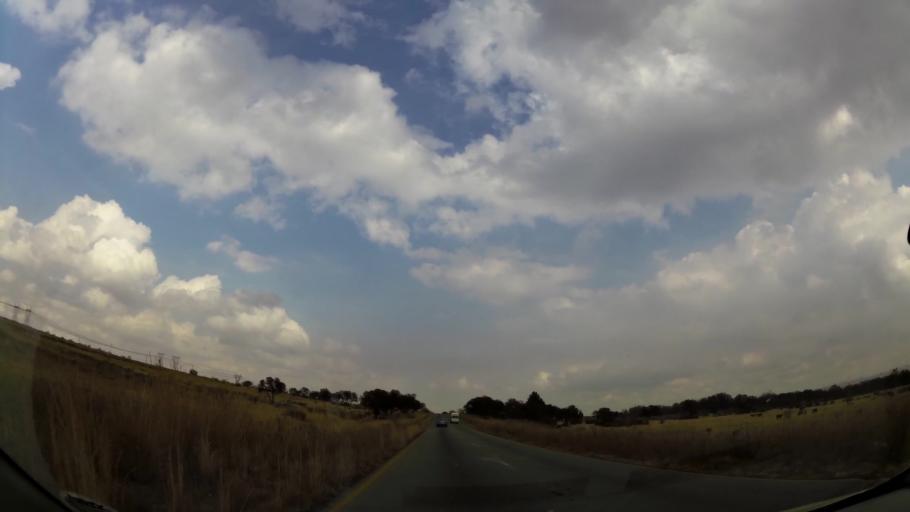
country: ZA
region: Orange Free State
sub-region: Fezile Dabi District Municipality
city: Sasolburg
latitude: -26.7849
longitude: 27.9179
